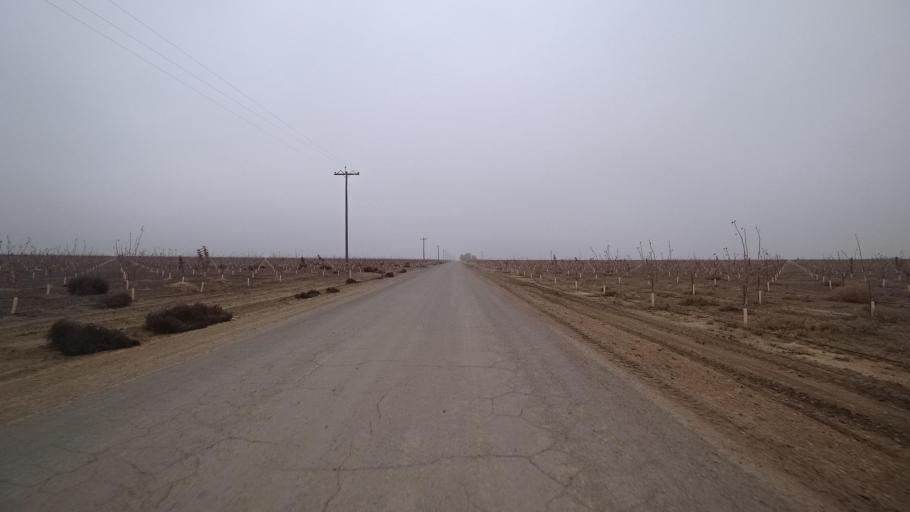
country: US
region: California
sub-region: Kern County
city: Wasco
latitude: 35.7099
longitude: -119.4194
